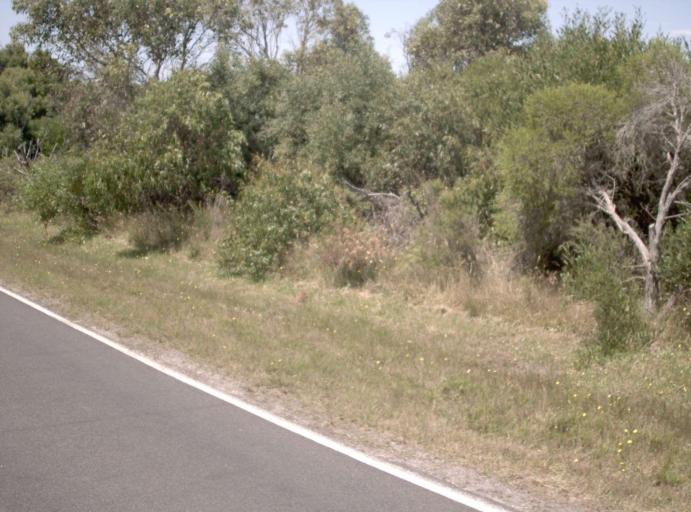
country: AU
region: Victoria
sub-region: Bass Coast
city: North Wonthaggi
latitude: -38.6794
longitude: 145.8730
